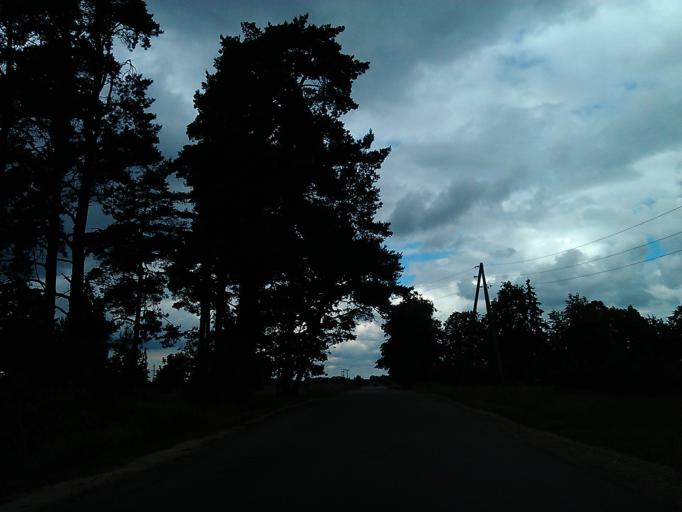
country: LV
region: Adazi
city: Adazi
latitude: 57.0873
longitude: 24.2994
